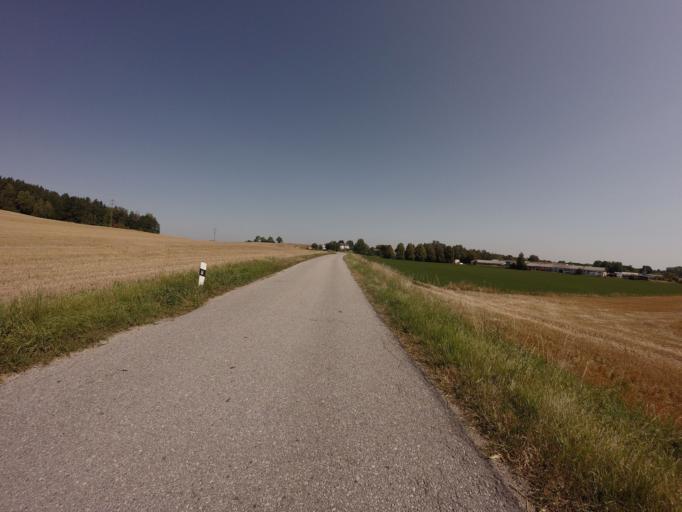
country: CZ
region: Jihocesky
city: Kamenny Ujezd
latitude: 48.8711
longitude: 14.3767
